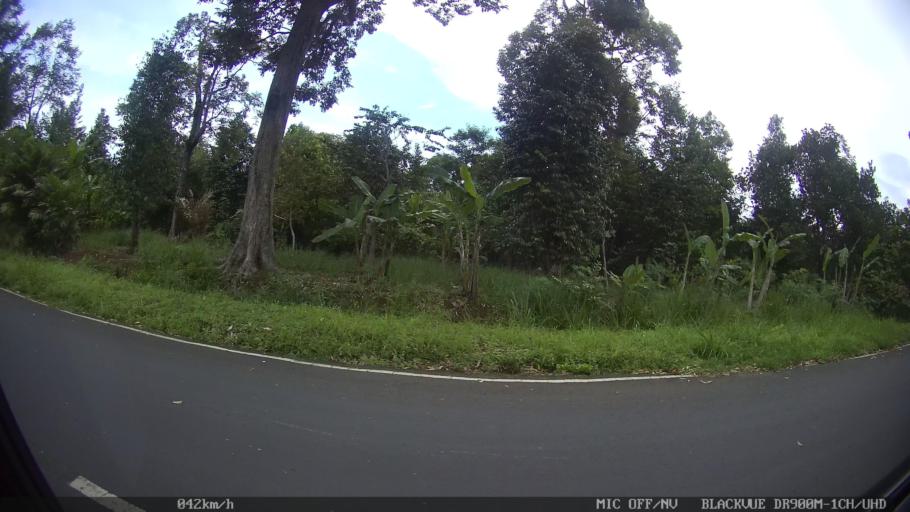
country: ID
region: Lampung
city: Bandarlampung
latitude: -5.4336
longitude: 105.2132
